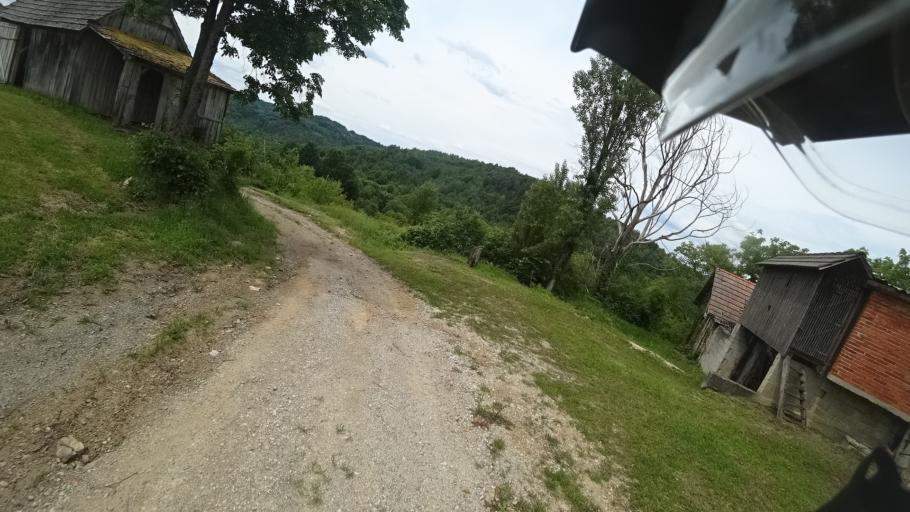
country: HR
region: Karlovacka
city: Vojnic
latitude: 45.2457
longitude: 15.6367
